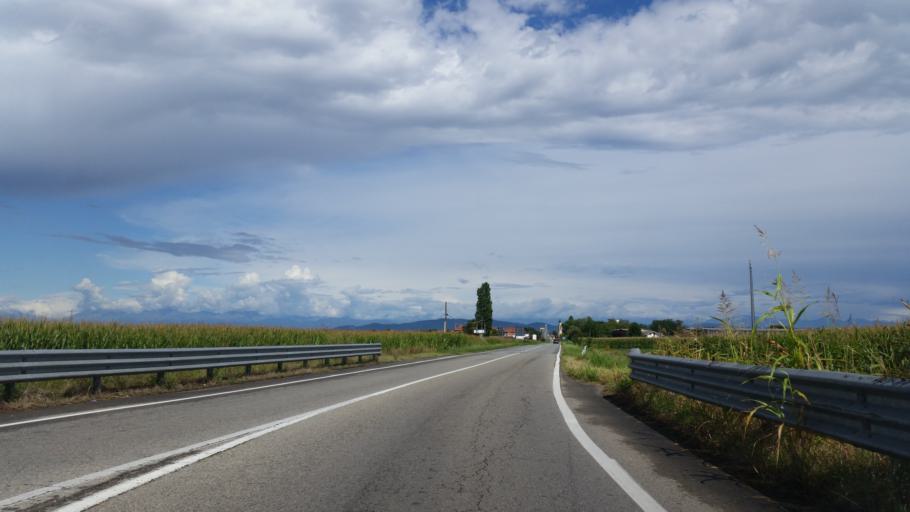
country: IT
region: Piedmont
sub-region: Provincia di Torino
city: Poirino
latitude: 44.9075
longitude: 7.8538
